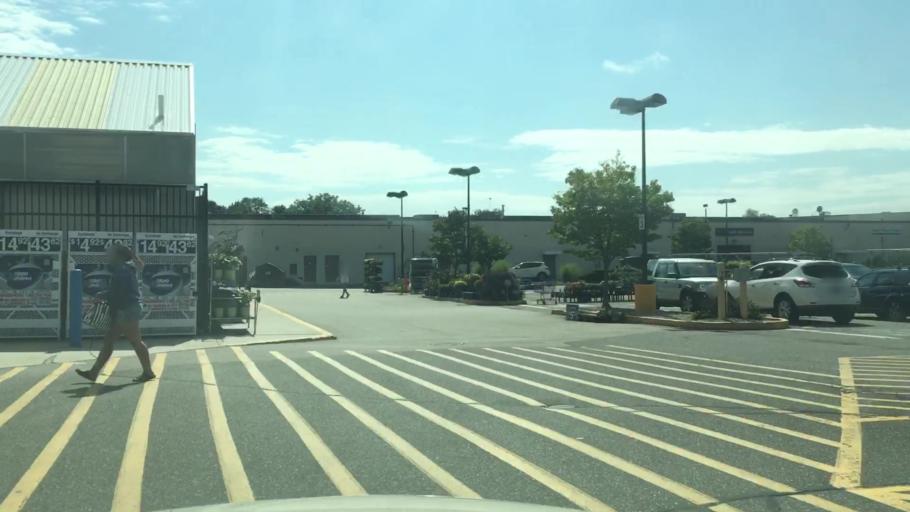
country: US
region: Connecticut
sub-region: Middlesex County
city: Old Saybrook
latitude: 41.2974
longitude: -72.3818
